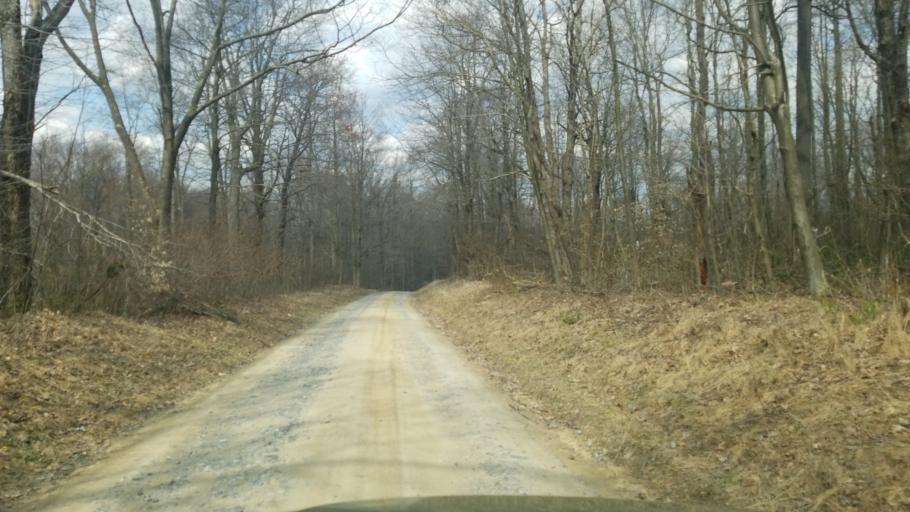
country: US
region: Pennsylvania
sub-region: Clearfield County
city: Clearfield
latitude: 41.1458
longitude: -78.5196
